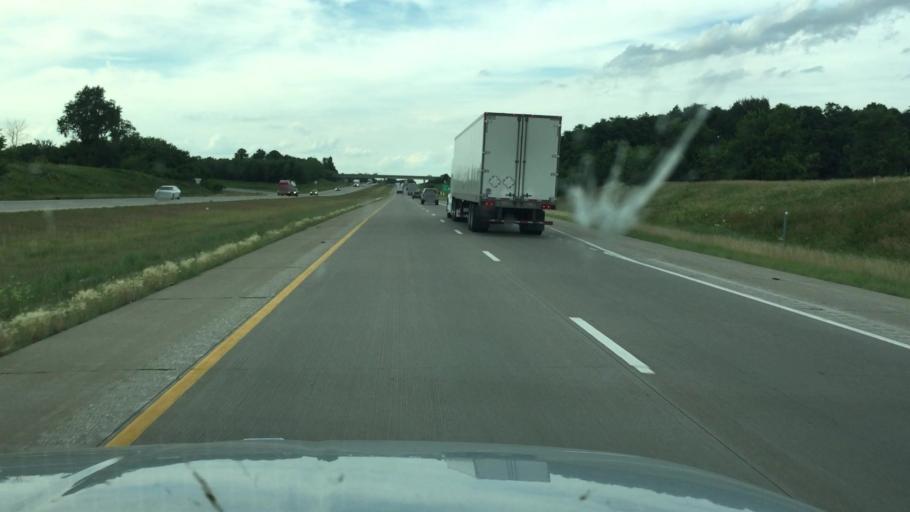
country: US
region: Iowa
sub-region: Scott County
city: Buffalo
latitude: 41.5325
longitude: -90.6752
